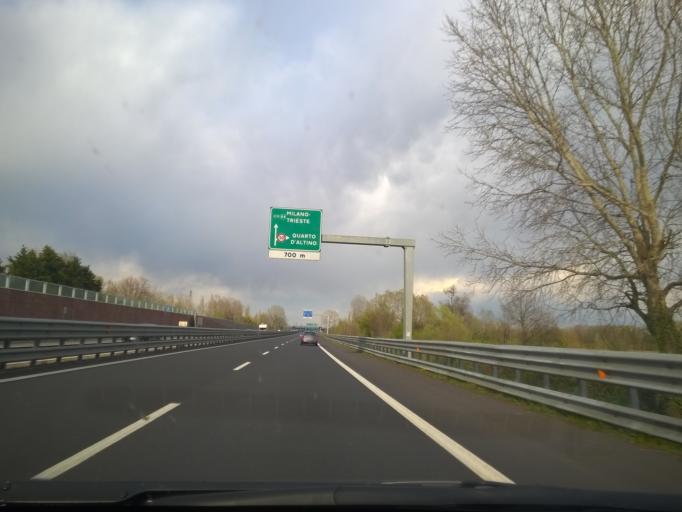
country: IT
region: Veneto
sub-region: Provincia di Venezia
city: San Liberale
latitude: 45.5624
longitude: 12.3238
